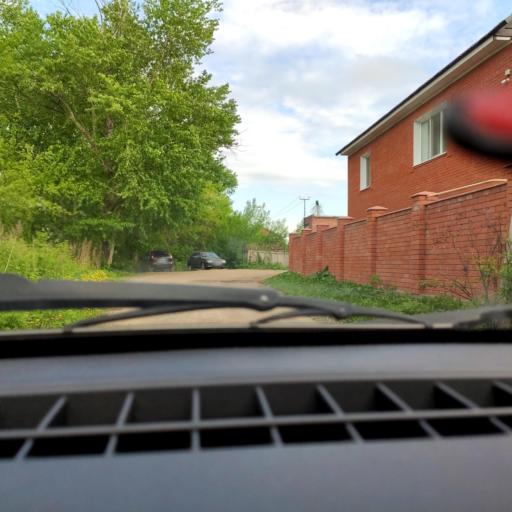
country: RU
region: Bashkortostan
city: Ufa
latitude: 54.7100
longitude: 55.9426
